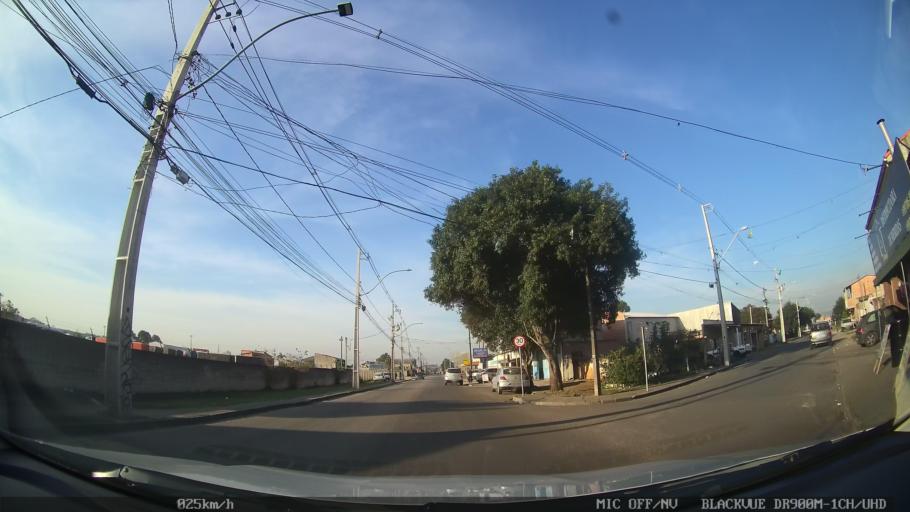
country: BR
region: Parana
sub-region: Pinhais
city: Pinhais
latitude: -25.4515
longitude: -49.1477
